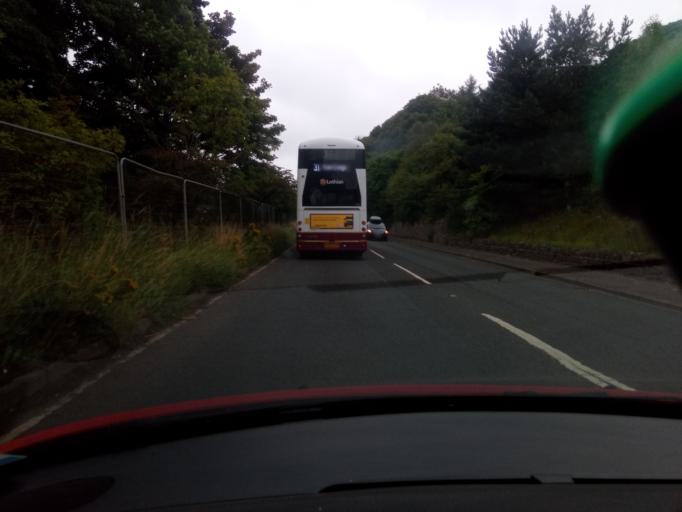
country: GB
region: Scotland
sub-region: Midlothian
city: Bonnyrigg
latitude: 55.8837
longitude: -3.1207
